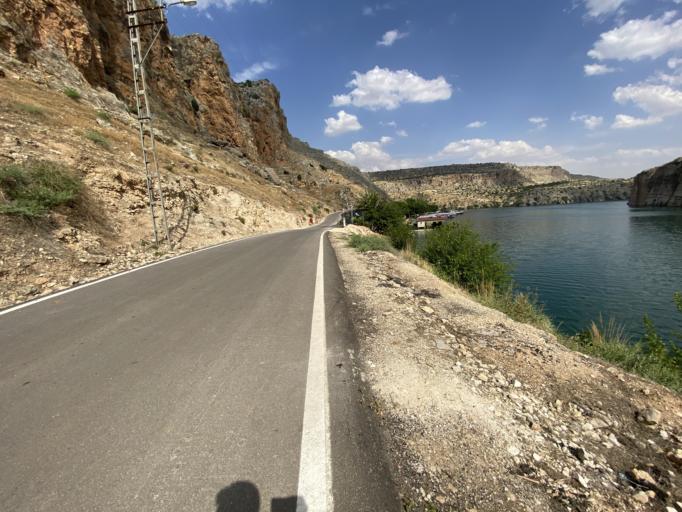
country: TR
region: Sanliurfa
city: Halfeti
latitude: 37.2751
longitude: 37.8369
